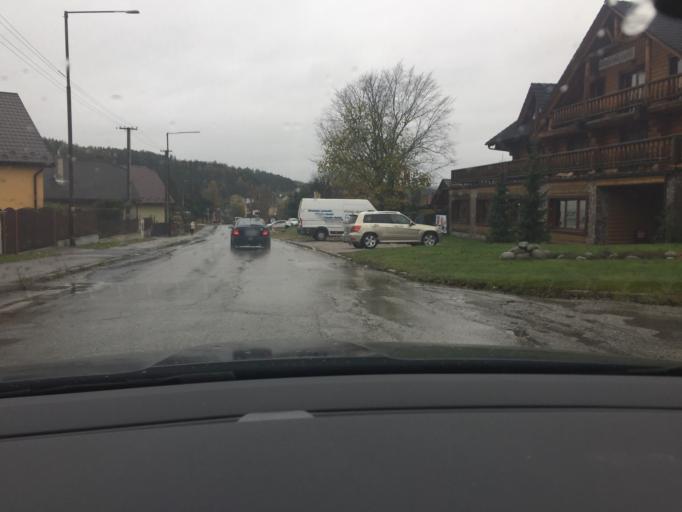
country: SK
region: Presovsky
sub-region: Okres Presov
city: Kezmarok
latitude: 49.1507
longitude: 20.4284
